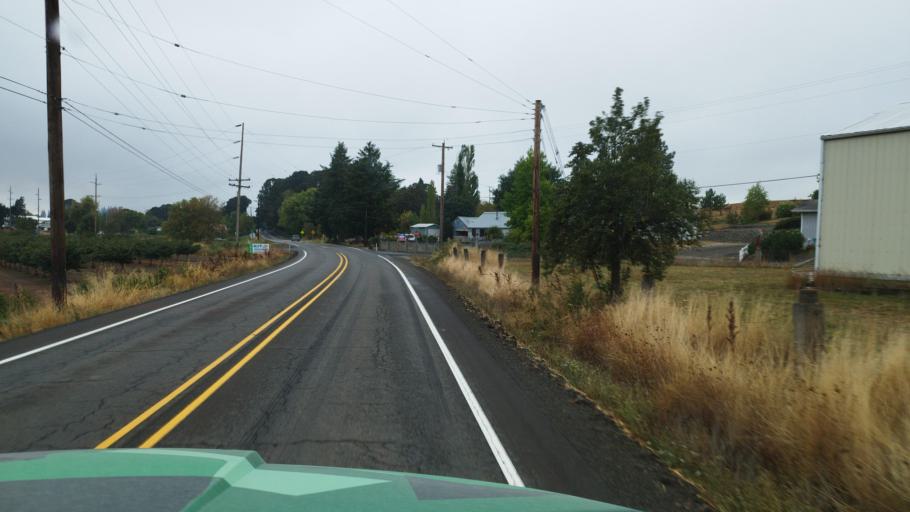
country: US
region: Oregon
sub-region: Yamhill County
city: Yamhill
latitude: 45.3510
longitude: -123.1745
